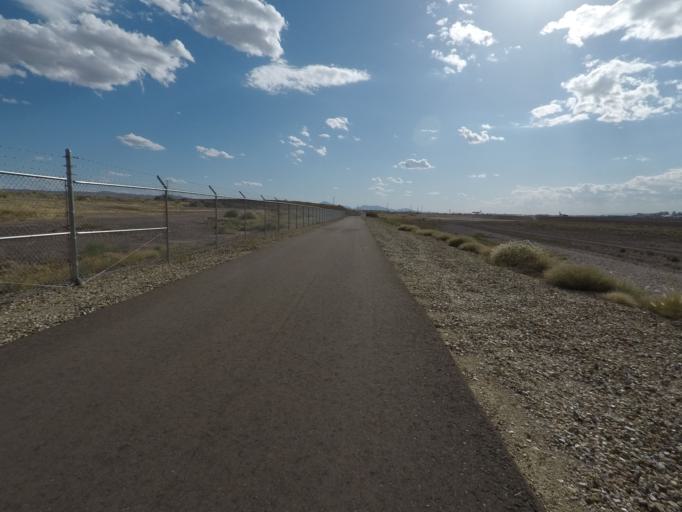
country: US
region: Arizona
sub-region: Maricopa County
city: Tempe Junction
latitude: 33.4295
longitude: -111.9836
